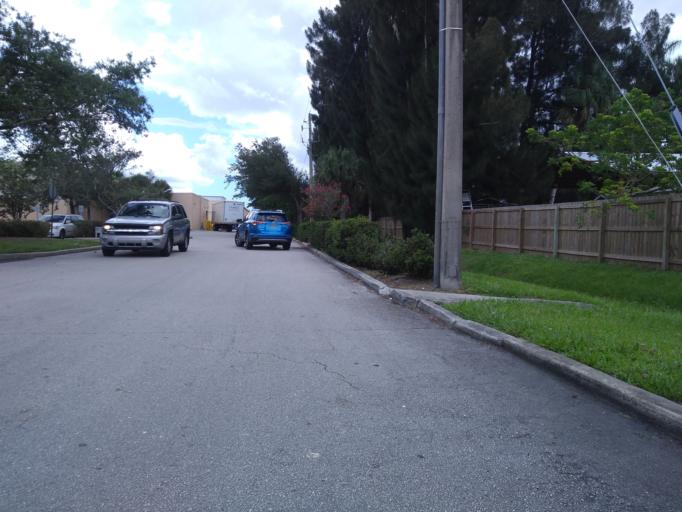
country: US
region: Florida
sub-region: Indian River County
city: Vero Beach South
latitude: 27.6390
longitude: -80.4447
